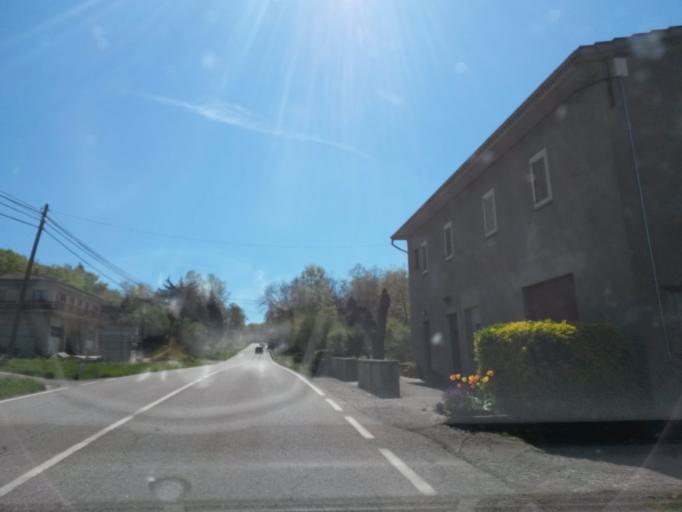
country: ES
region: Catalonia
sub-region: Provincia de Girona
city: Sant Cristofol de les Fonts
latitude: 42.1673
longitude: 2.5048
